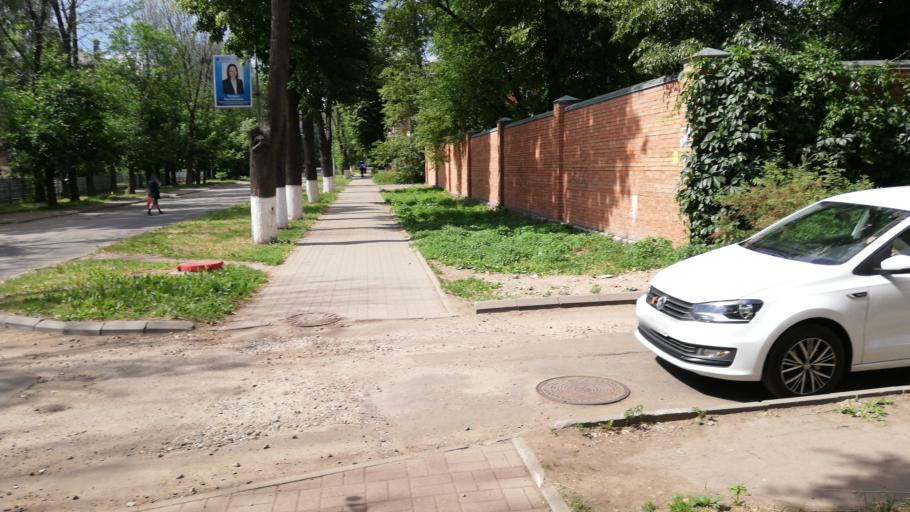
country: RU
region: Jaroslavl
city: Yaroslavl
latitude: 57.6393
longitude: 39.8702
